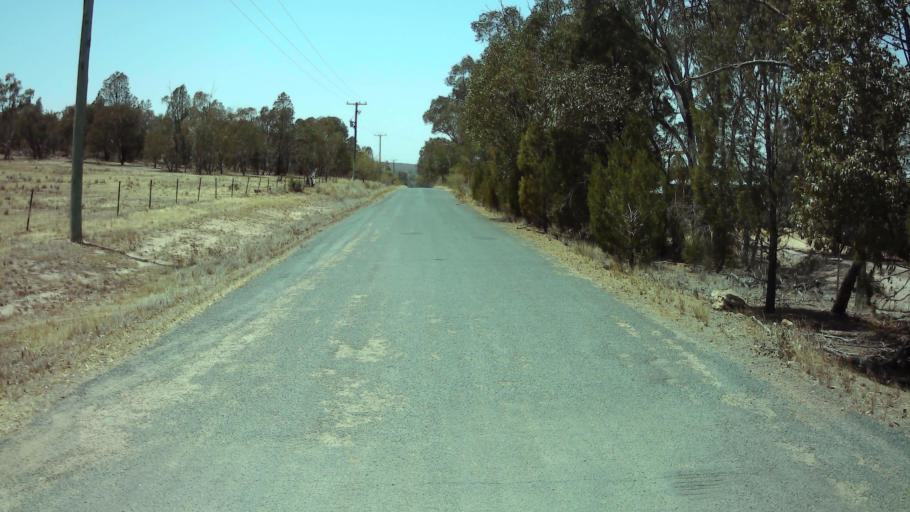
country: AU
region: New South Wales
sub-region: Weddin
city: Grenfell
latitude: -33.8883
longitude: 148.1448
